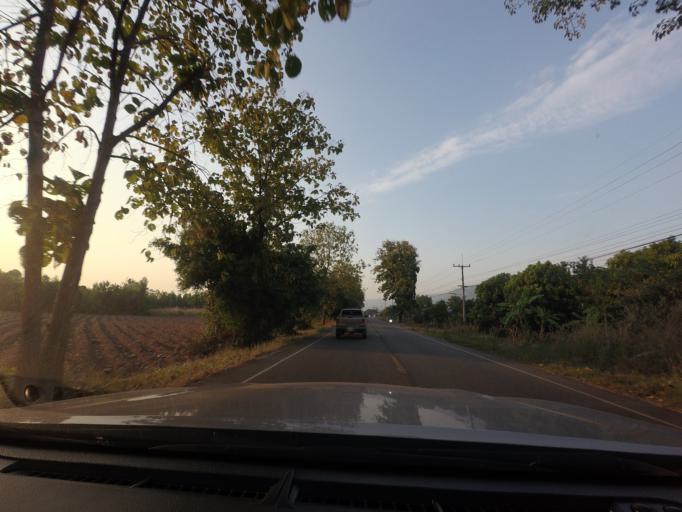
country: TH
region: Phitsanulok
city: Wang Thong
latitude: 16.7018
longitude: 100.5151
